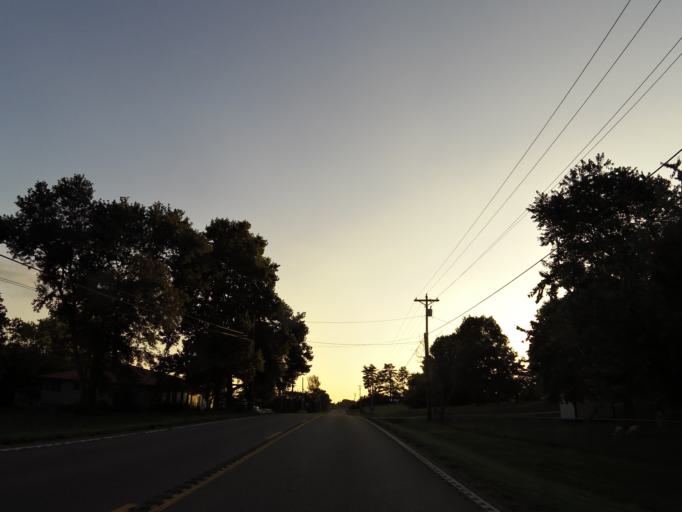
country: US
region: Tennessee
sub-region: Jefferson County
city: New Market
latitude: 36.0224
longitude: -83.5939
